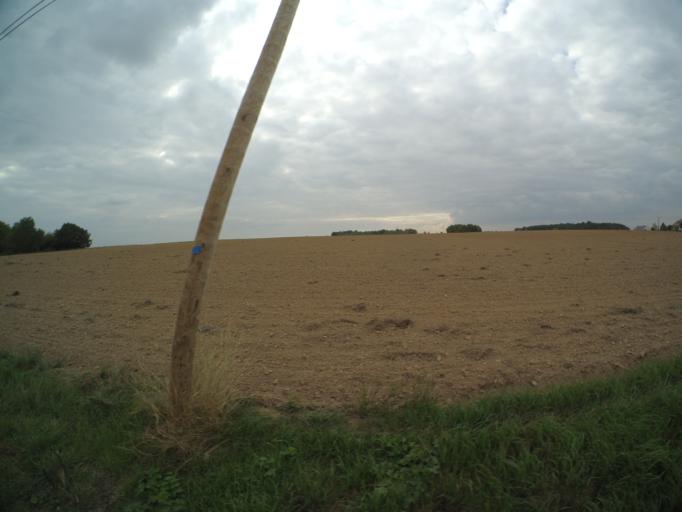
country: FR
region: Centre
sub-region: Departement d'Indre-et-Loire
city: Poce-sur-Cisse
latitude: 47.4989
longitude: 0.9750
